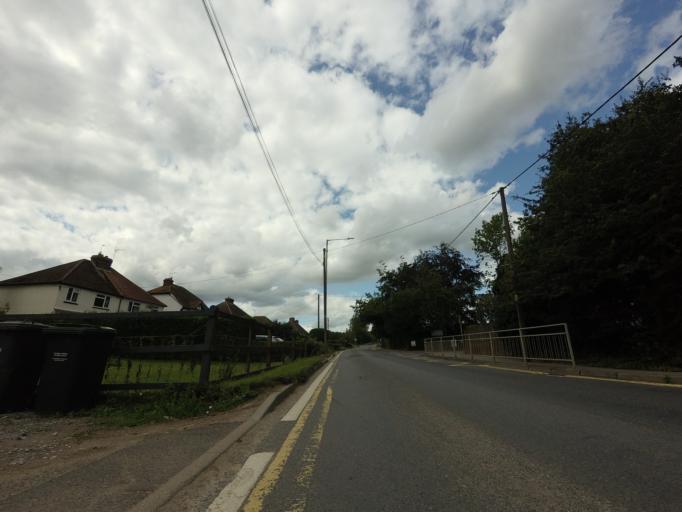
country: GB
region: England
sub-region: Kent
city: Borough Green
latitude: 51.2997
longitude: 0.3094
